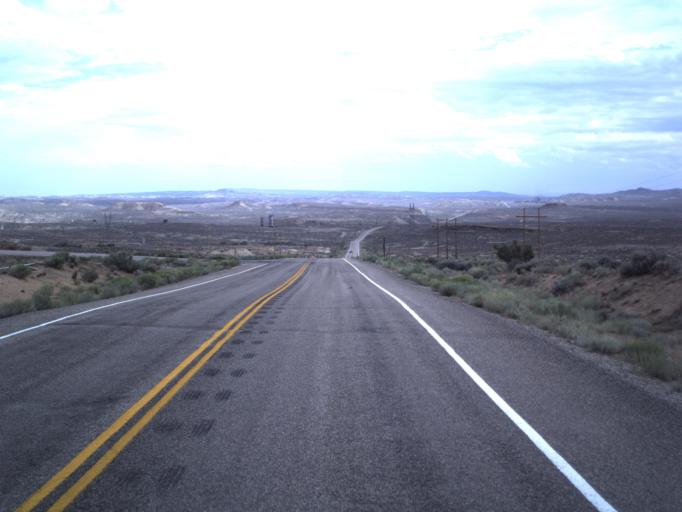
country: US
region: Colorado
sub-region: Rio Blanco County
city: Rangely
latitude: 40.0777
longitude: -109.2100
